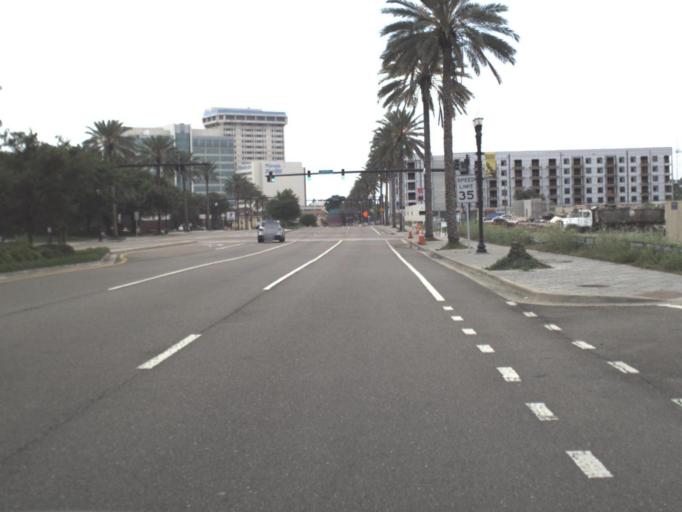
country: US
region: Florida
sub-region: Duval County
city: Jacksonville
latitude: 30.3240
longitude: -81.6701
